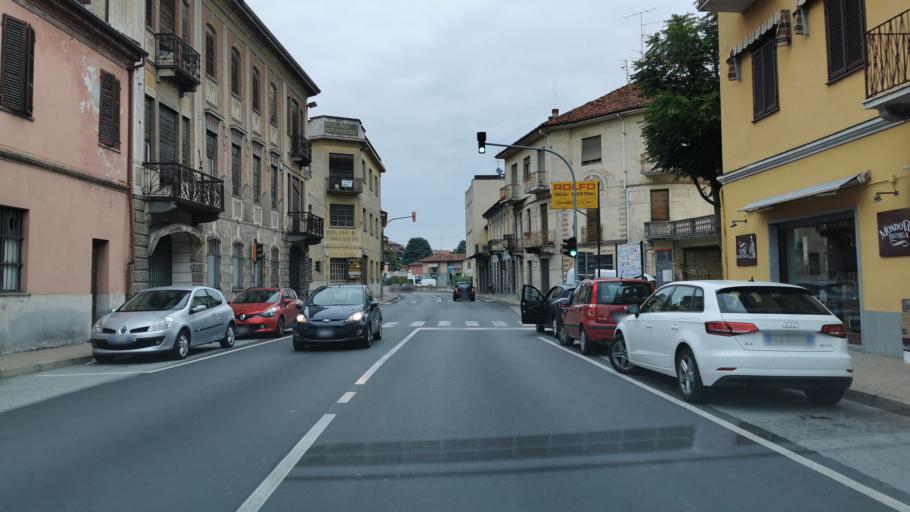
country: IT
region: Piedmont
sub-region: Provincia di Cuneo
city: Bra
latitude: 44.6887
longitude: 7.8541
